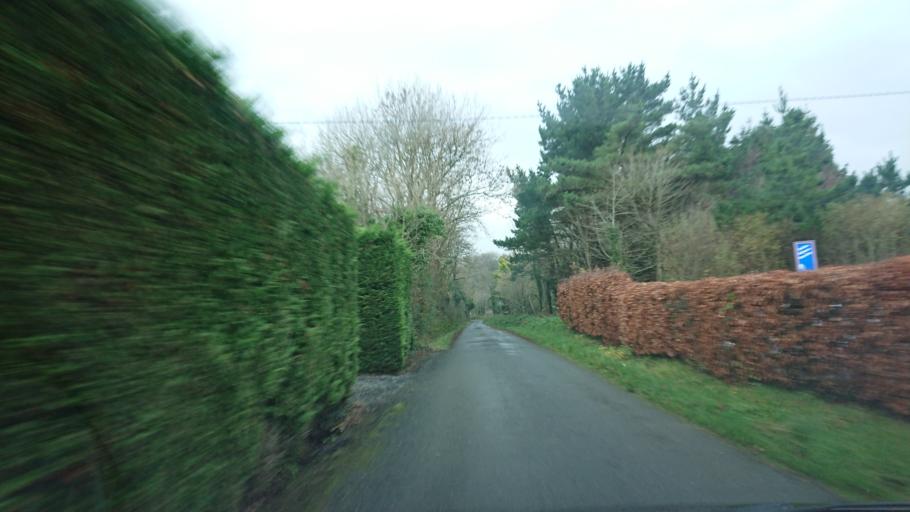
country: IE
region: Munster
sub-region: Waterford
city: Dunmore East
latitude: 52.1979
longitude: -7.0137
